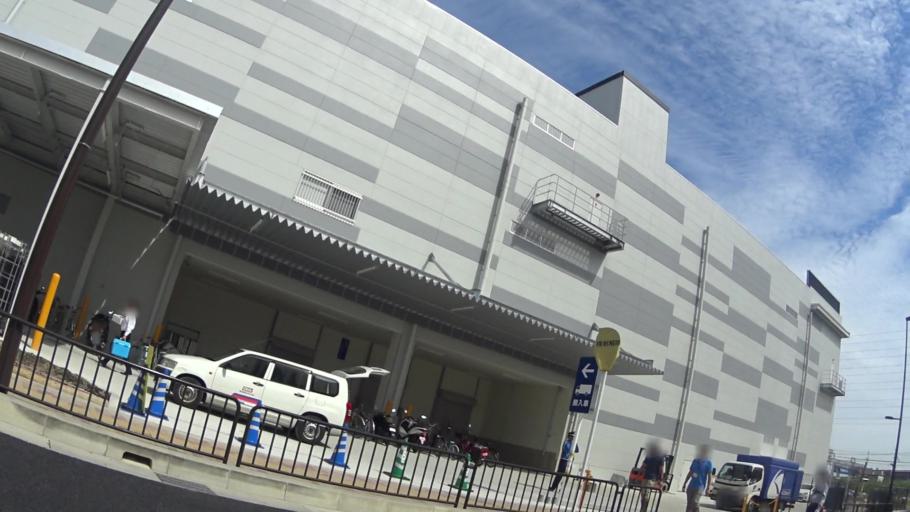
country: JP
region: Kyoto
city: Muko
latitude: 34.9632
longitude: 135.7090
